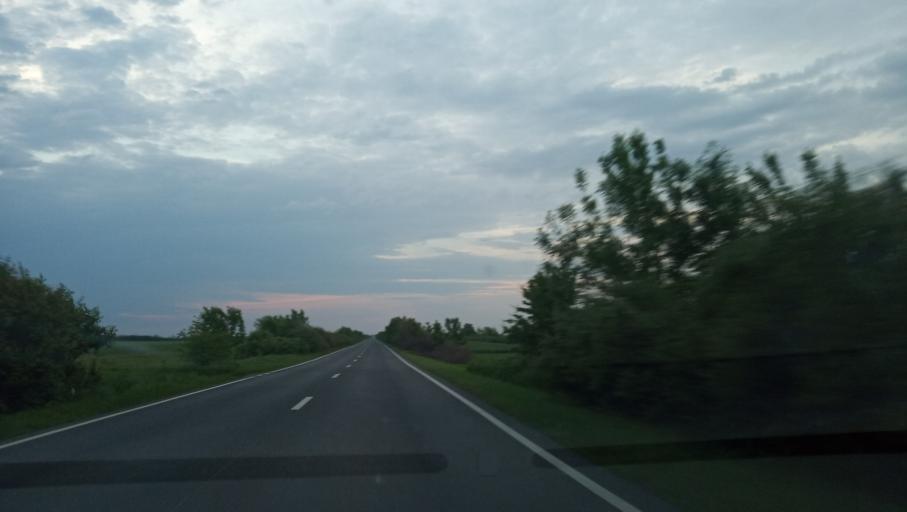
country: RO
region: Timis
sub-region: Comuna Jebel
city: Jebel
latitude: 45.5286
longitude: 21.2305
